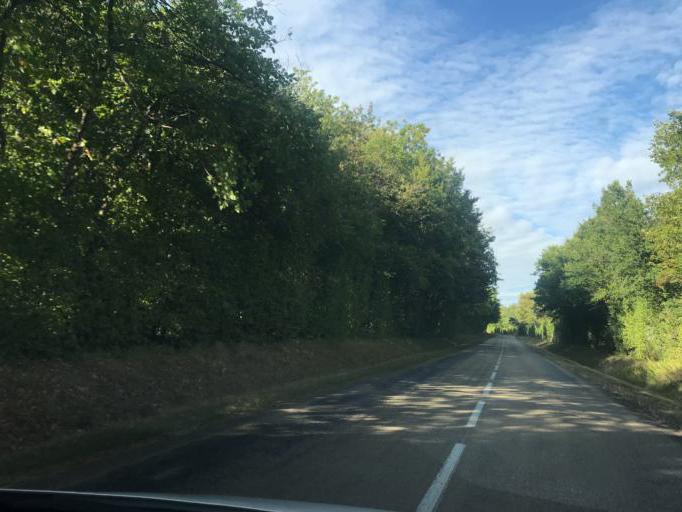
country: FR
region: Bourgogne
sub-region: Departement de l'Yonne
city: Fontenailles
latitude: 47.5704
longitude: 3.4522
